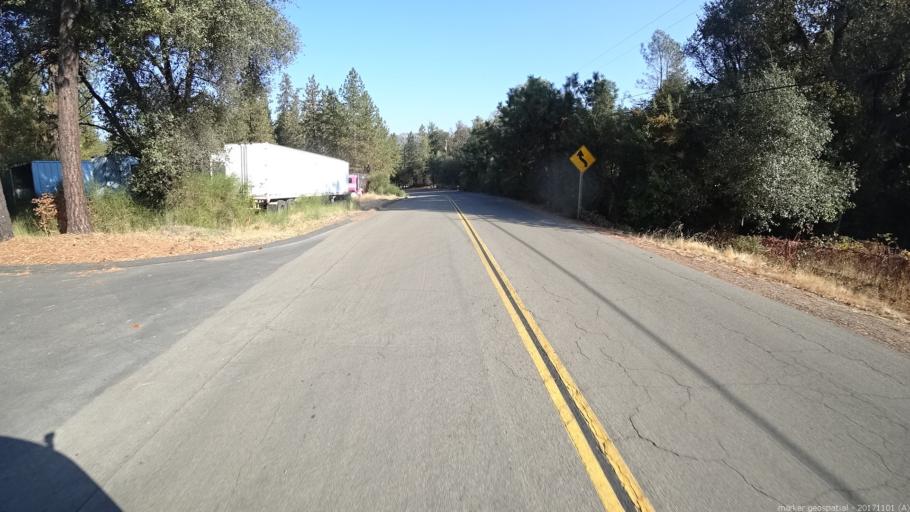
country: US
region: California
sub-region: Shasta County
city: Shasta Lake
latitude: 40.7264
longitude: -122.3211
